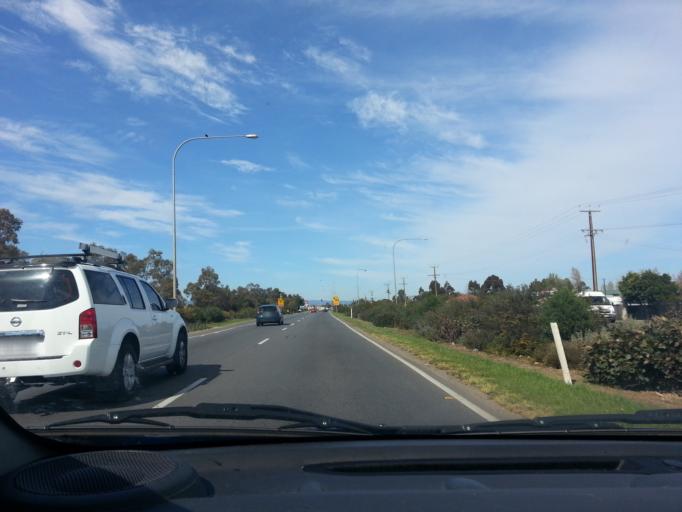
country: AU
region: South Australia
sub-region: Salisbury
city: Salisbury
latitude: -34.7291
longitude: 138.5816
